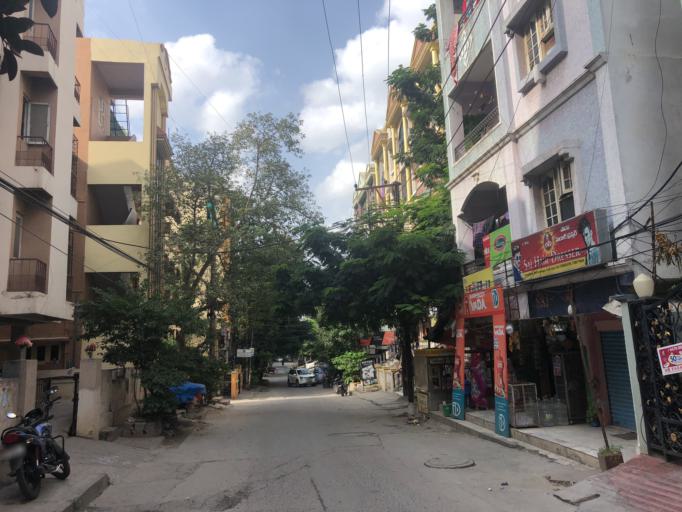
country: IN
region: Telangana
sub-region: Rangareddi
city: Kukatpalli
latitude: 17.4376
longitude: 78.4326
